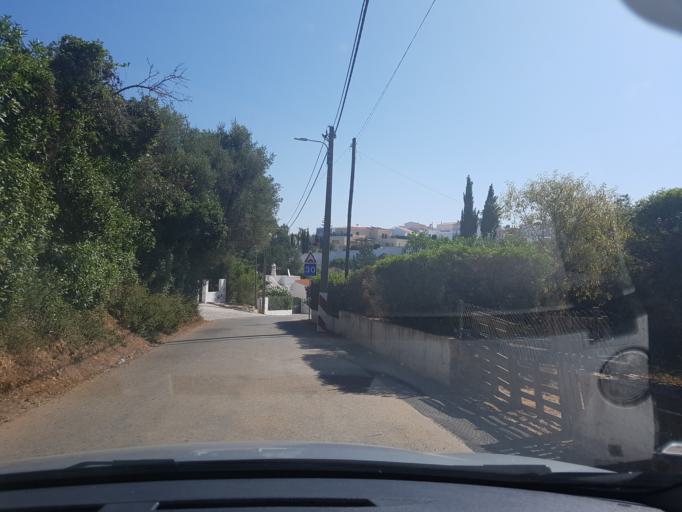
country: PT
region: Faro
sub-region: Lagoa
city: Carvoeiro
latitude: 37.0988
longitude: -8.4622
